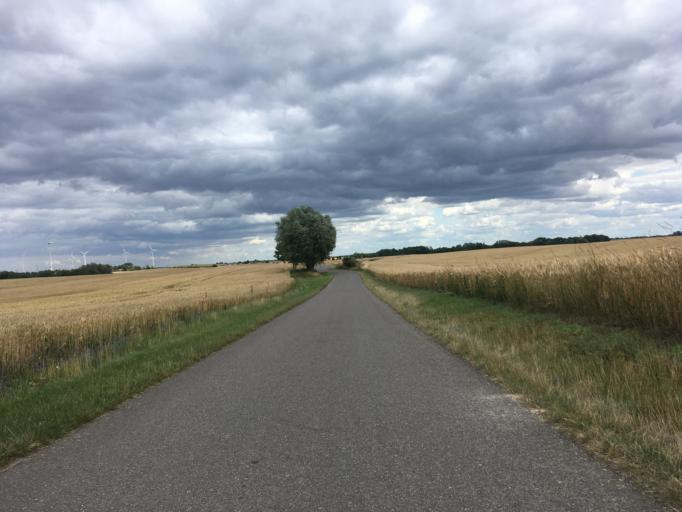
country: DE
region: Brandenburg
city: Gramzow
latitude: 53.2574
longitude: 13.9837
